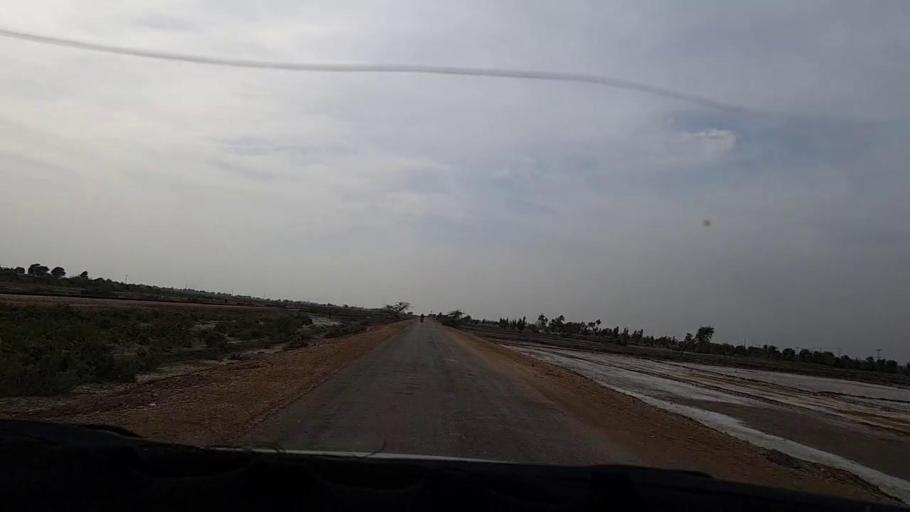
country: PK
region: Sindh
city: Pithoro
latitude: 25.5165
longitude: 69.2727
